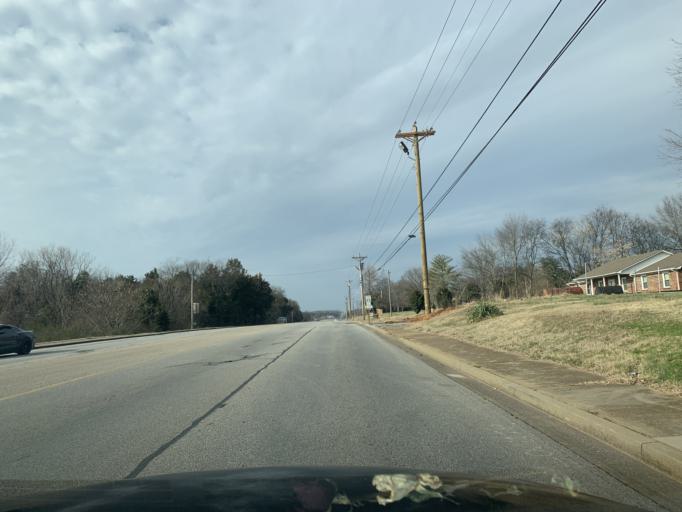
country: US
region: Tennessee
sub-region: Rutherford County
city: Smyrna
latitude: 35.9494
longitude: -86.5095
